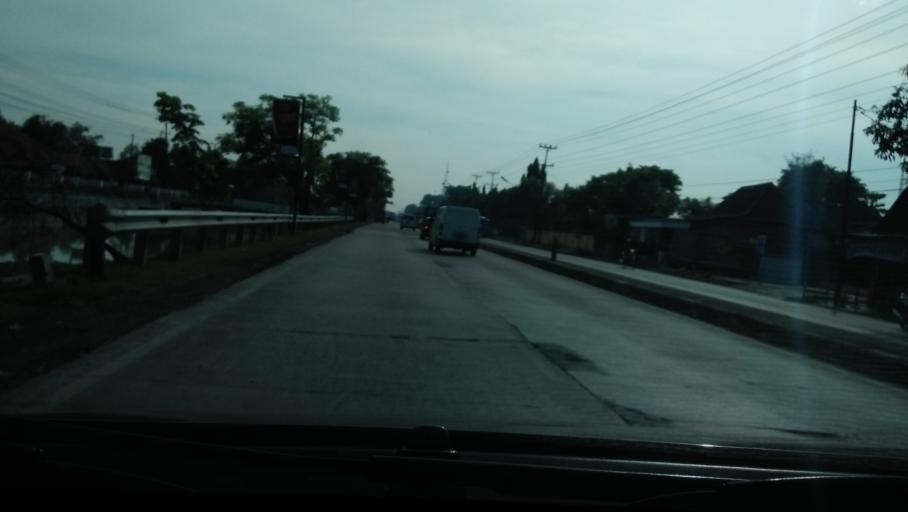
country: ID
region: Central Java
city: Demak
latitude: -6.9272
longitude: 110.5539
